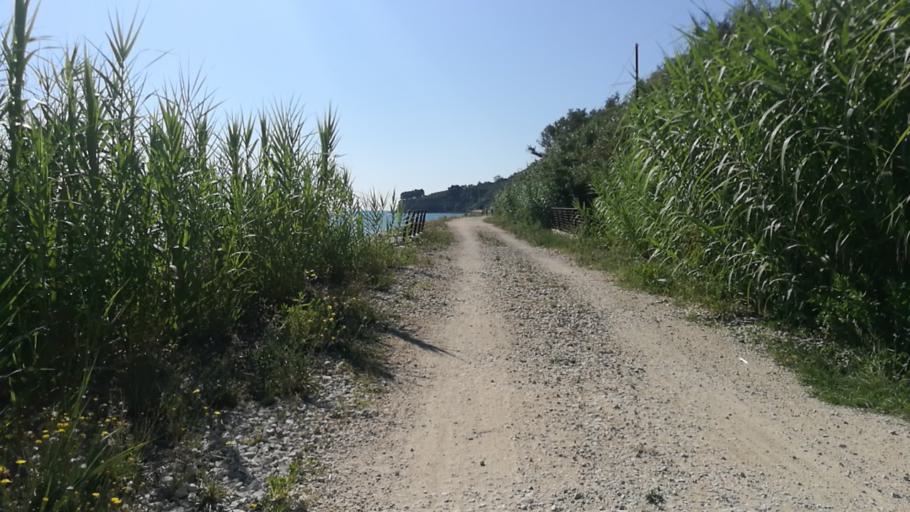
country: IT
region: Abruzzo
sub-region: Provincia di Chieti
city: Ortona
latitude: 42.3421
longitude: 14.4138
